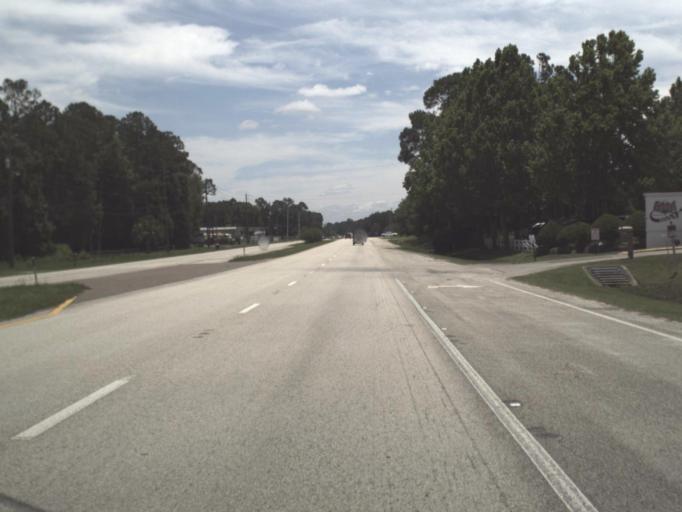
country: US
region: Florida
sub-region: Nassau County
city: Nassau Village-Ratliff
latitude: 30.4520
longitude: -81.7704
